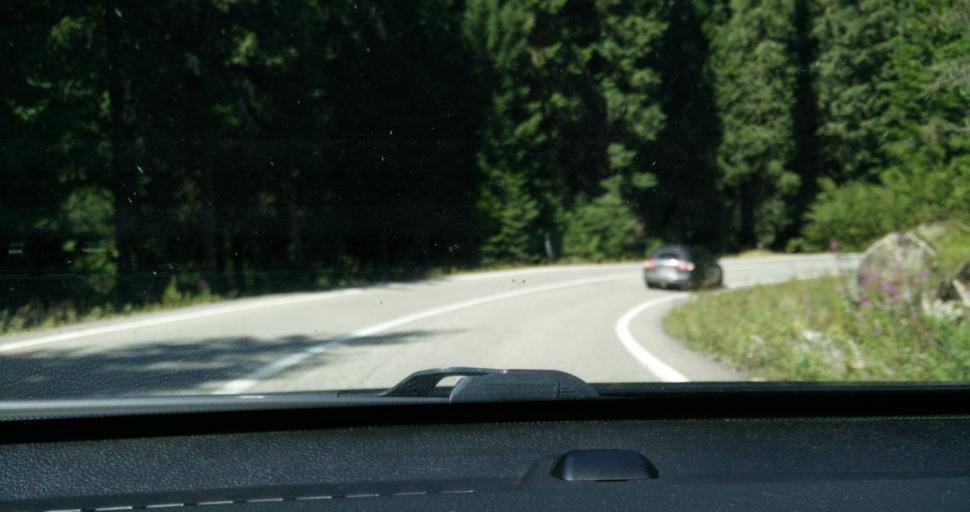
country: RO
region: Hunedoara
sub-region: Oras Petrila
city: Petrila
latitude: 45.5201
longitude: 23.6501
